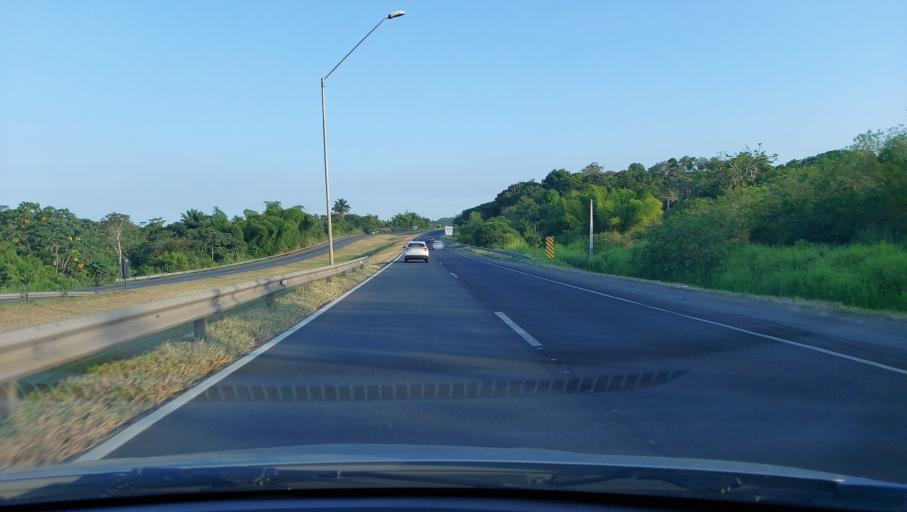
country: BR
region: Bahia
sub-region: Sao Sebastiao Do Passe
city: Sao Sebastiao do Passe
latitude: -12.6121
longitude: -38.4894
